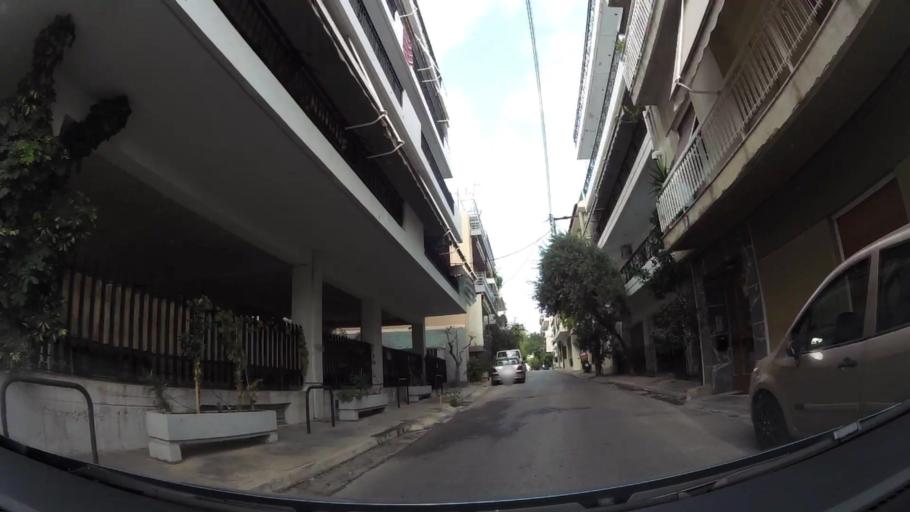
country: GR
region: Attica
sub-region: Nomarchia Athinas
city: Petroupolis
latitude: 38.0434
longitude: 23.6939
